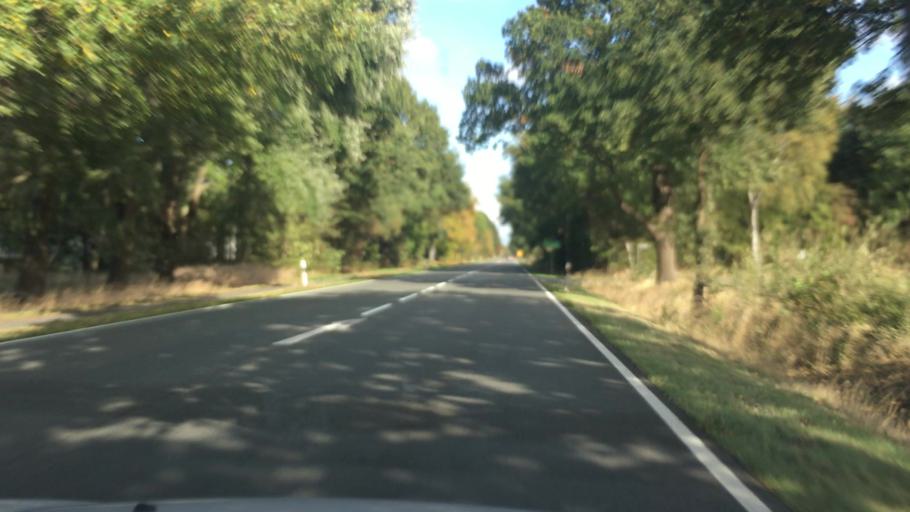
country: DE
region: Lower Saxony
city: Freistatt
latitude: 52.6190
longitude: 8.6443
